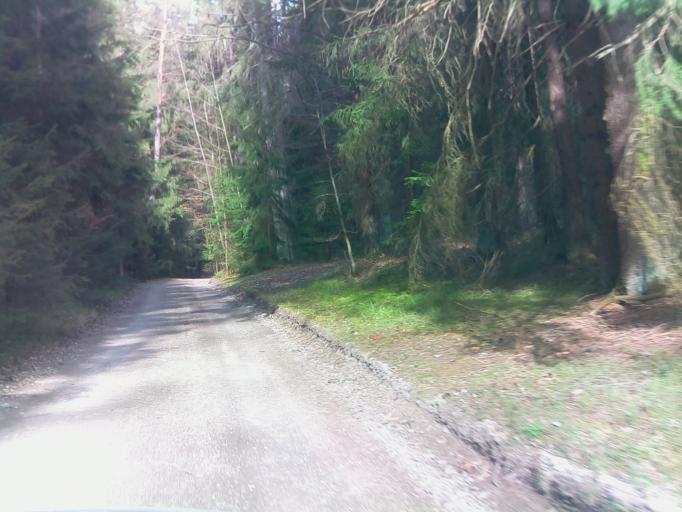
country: DE
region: Bavaria
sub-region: Upper Palatinate
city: Freudenberg
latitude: 49.4700
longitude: 12.0109
